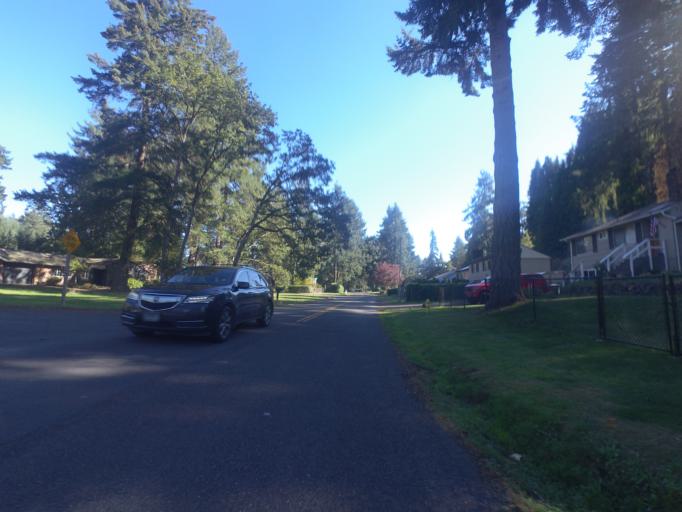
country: US
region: Washington
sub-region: Pierce County
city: Lakewood
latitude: 47.1468
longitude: -122.5186
